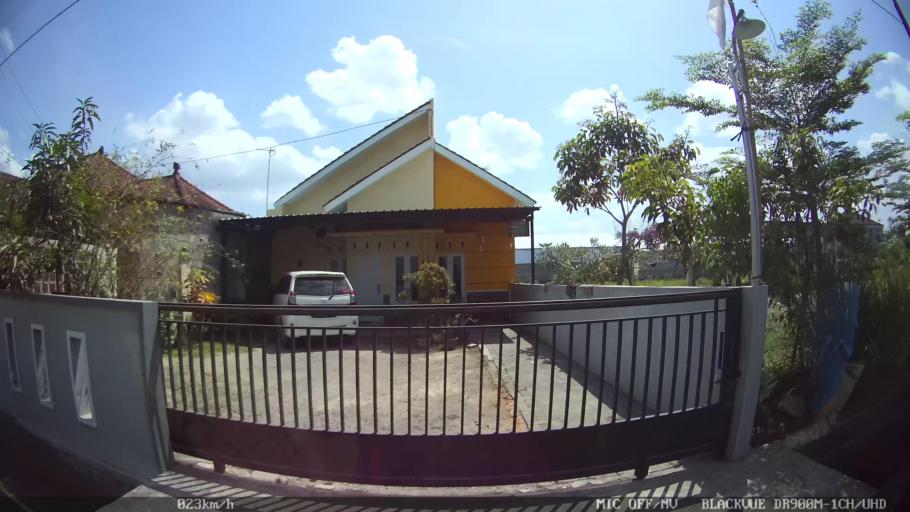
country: ID
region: Daerah Istimewa Yogyakarta
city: Sewon
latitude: -7.8476
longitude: 110.3883
